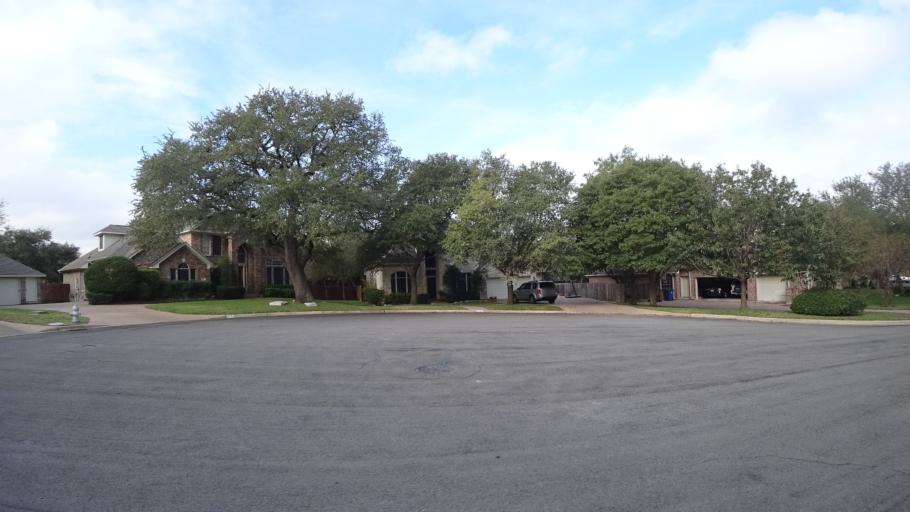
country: US
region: Texas
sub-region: Travis County
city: Shady Hollow
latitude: 30.1934
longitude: -97.8775
